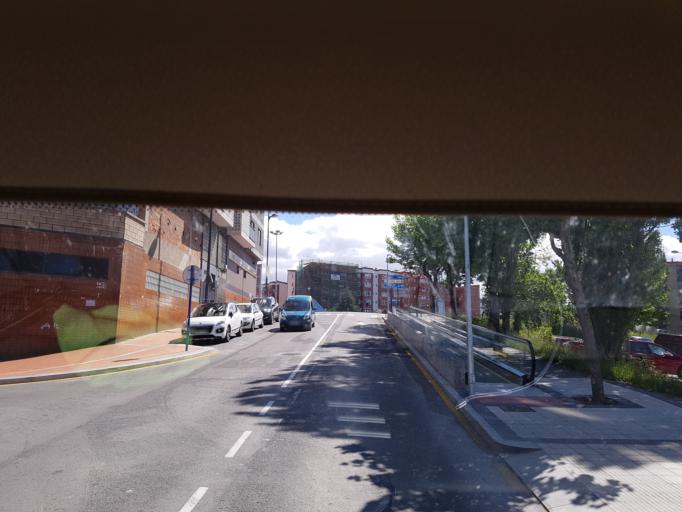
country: ES
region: Basque Country
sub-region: Bizkaia
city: Barakaldo
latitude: 43.2866
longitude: -2.9824
